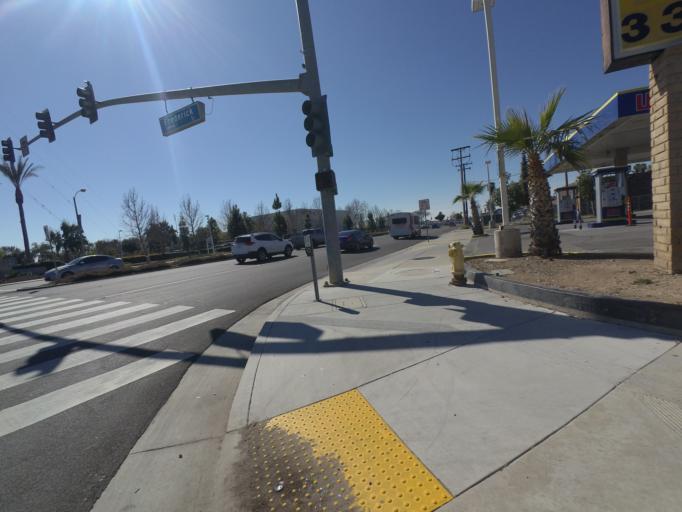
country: US
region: California
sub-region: Riverside County
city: March Air Force Base
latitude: 33.9174
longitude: -117.2613
